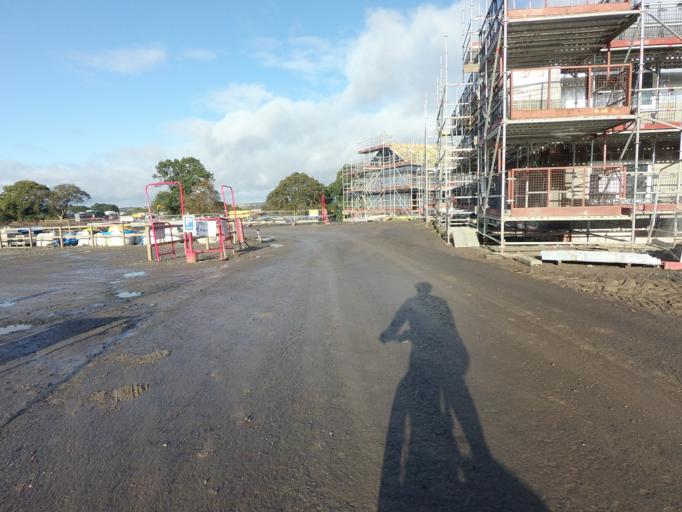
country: GB
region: Scotland
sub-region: West Lothian
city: Livingston
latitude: 55.8684
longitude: -3.5361
